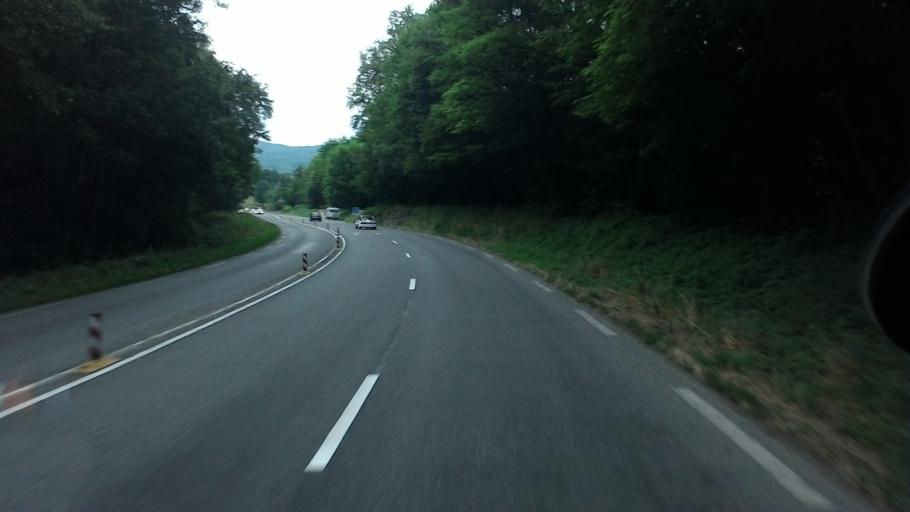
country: FR
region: Rhone-Alpes
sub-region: Departement de la Savoie
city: Yenne
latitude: 45.7037
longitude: 5.7834
